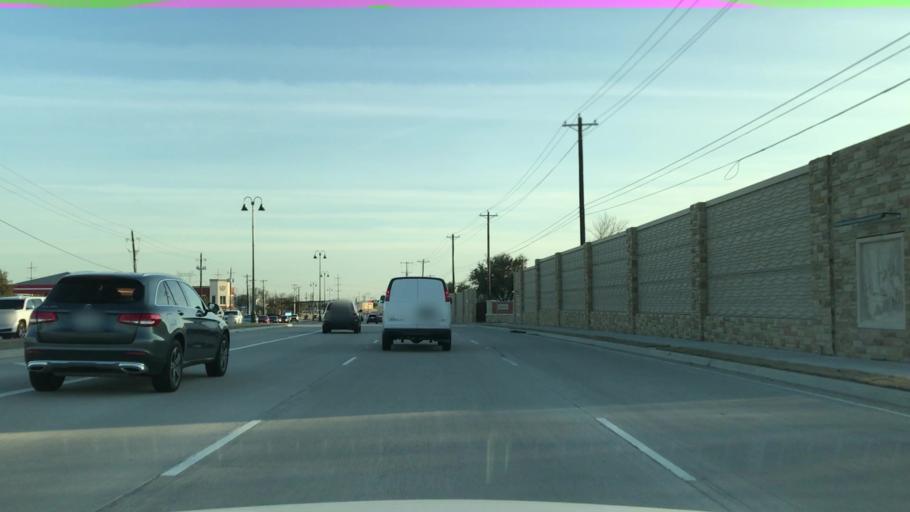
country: US
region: Texas
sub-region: Denton County
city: The Colony
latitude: 33.0769
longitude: -96.8929
